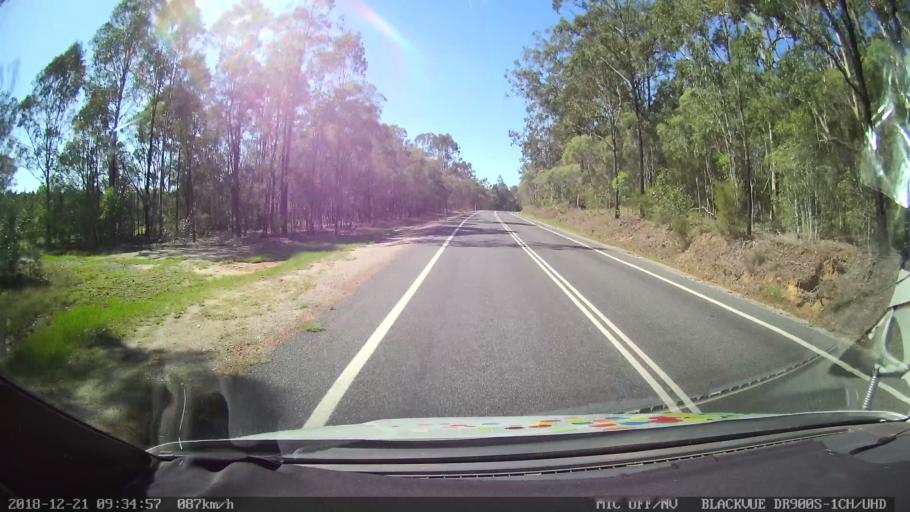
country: AU
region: New South Wales
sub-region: Clarence Valley
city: Grafton
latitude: -29.5044
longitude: 152.9821
